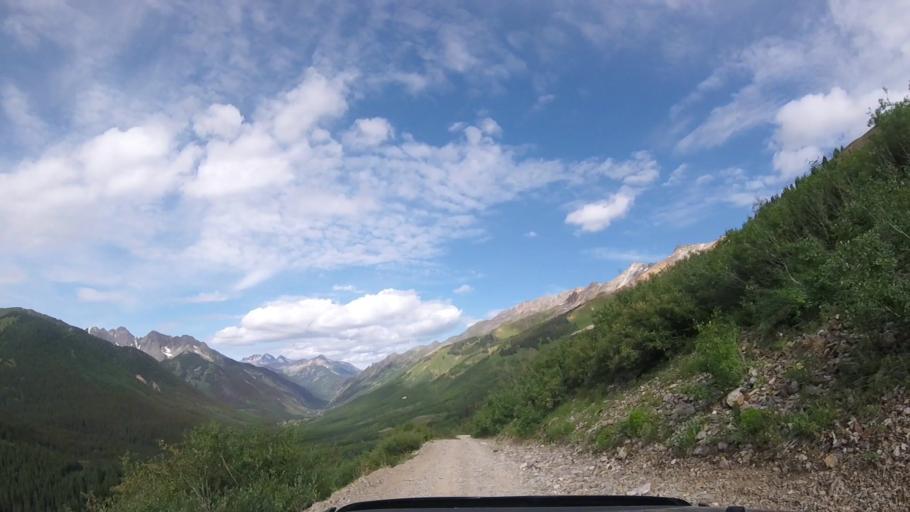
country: US
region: Colorado
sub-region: San Miguel County
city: Telluride
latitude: 37.8579
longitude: -107.7907
